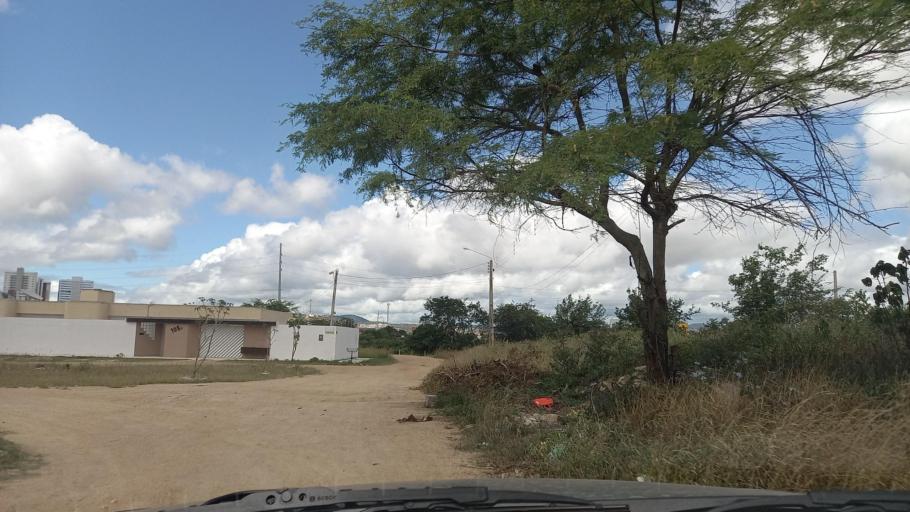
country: BR
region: Pernambuco
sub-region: Caruaru
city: Caruaru
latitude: -8.2595
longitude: -35.9796
